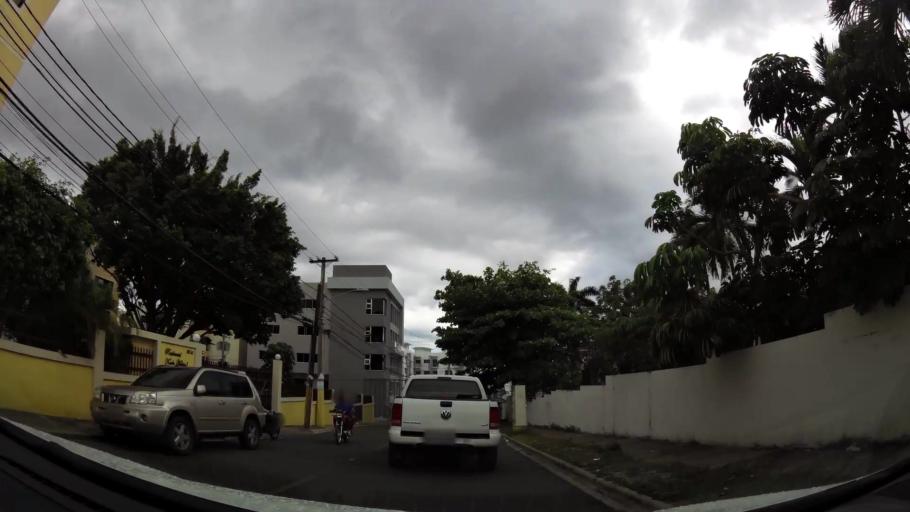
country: DO
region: Nacional
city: La Agustina
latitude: 18.4931
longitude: -69.9346
